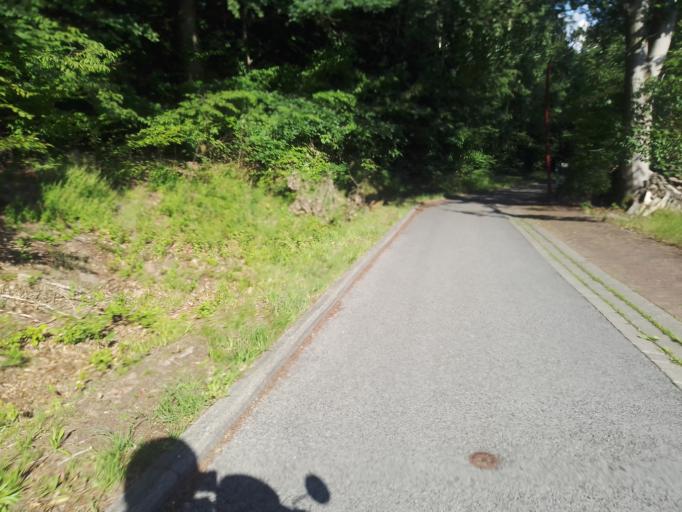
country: DE
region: Bavaria
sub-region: Regierungsbezirk Unterfranken
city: Hasloch
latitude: 49.8061
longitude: 9.4870
